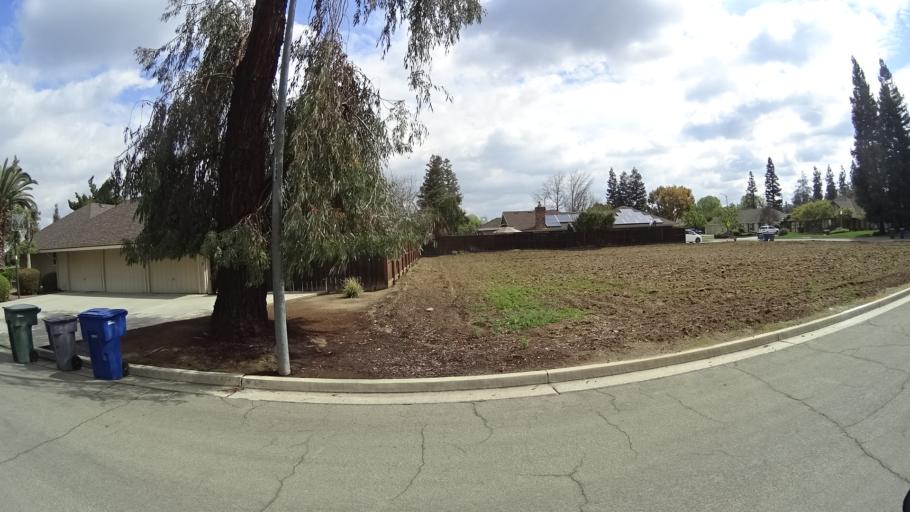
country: US
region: California
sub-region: Fresno County
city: Fresno
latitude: 36.8397
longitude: -119.8587
